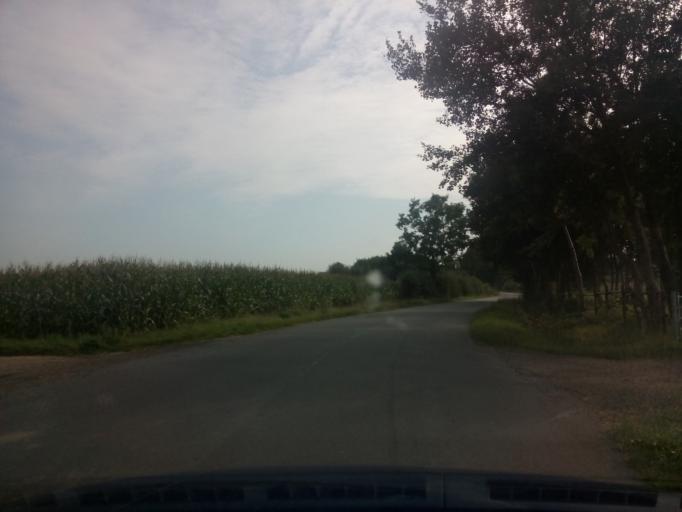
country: DE
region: Lower Saxony
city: Osterholz-Scharmbeck
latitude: 53.2477
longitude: 8.7586
